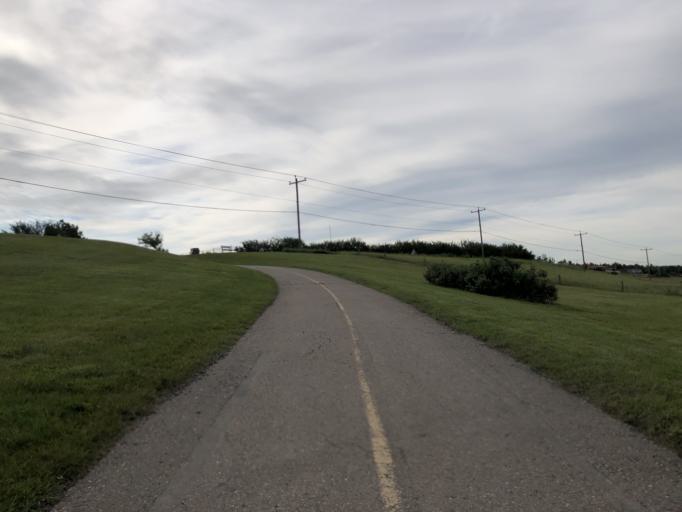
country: CA
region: Alberta
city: Calgary
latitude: 51.0743
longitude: -114.0260
